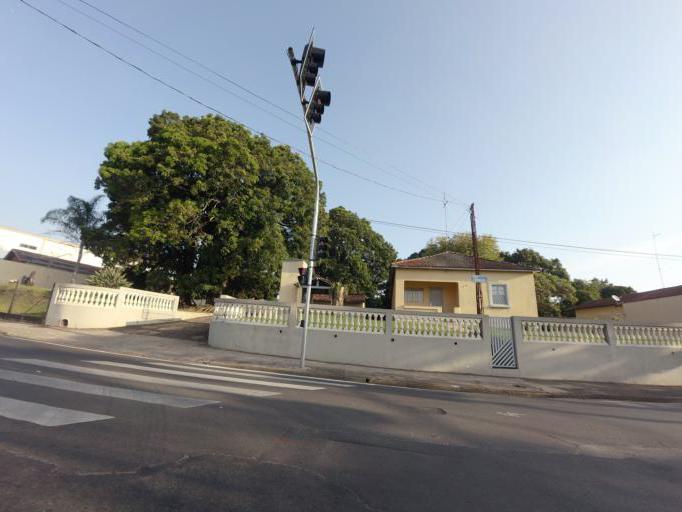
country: BR
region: Sao Paulo
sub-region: Piracicaba
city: Piracicaba
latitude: -22.7414
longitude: -47.6113
